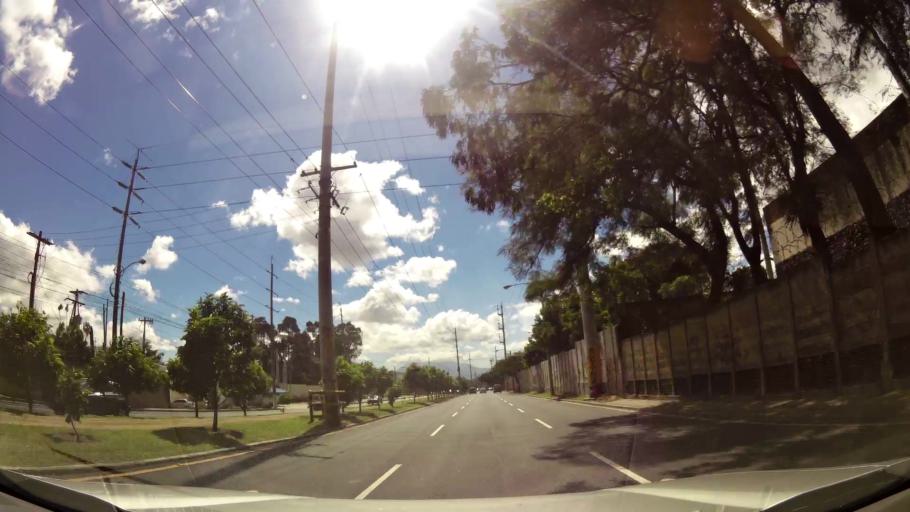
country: GT
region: Guatemala
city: Santa Catarina Pinula
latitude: 14.5686
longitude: -90.5437
